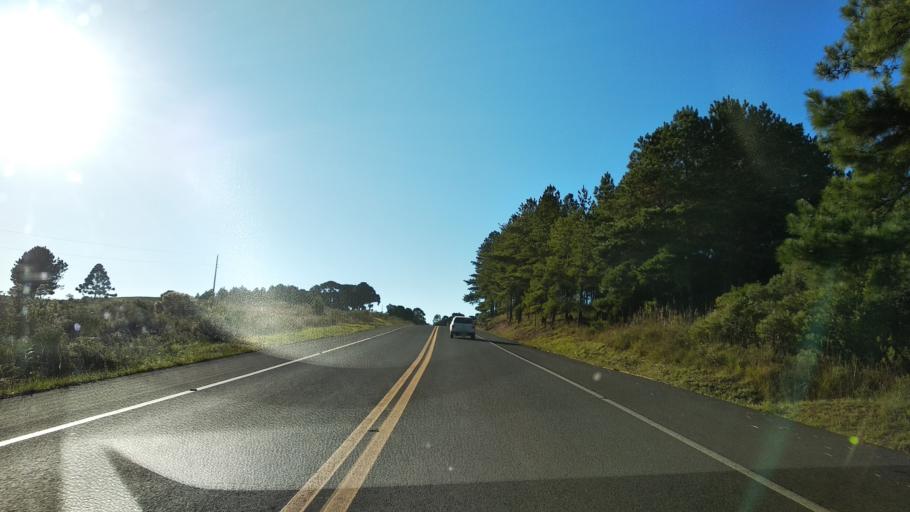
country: BR
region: Santa Catarina
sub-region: Lages
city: Lages
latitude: -27.7907
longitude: -50.4196
